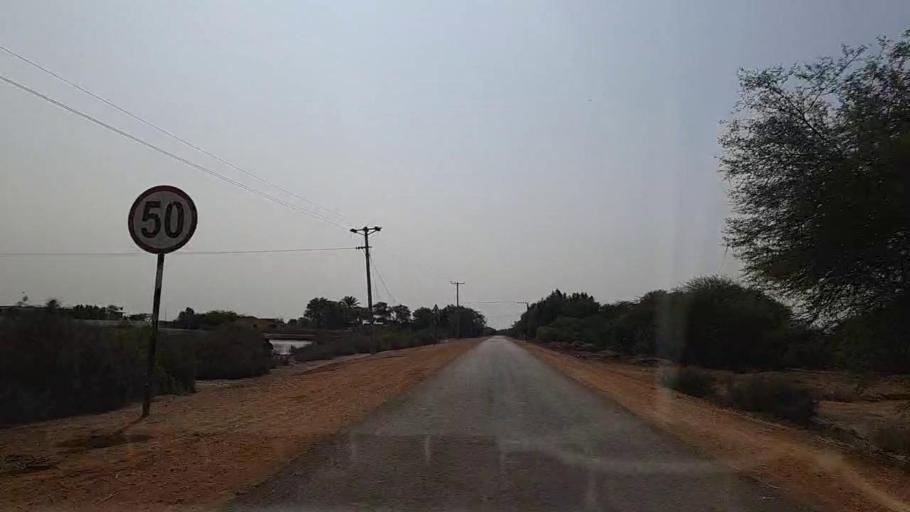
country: PK
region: Sindh
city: Chuhar Jamali
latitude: 24.3244
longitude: 67.9423
